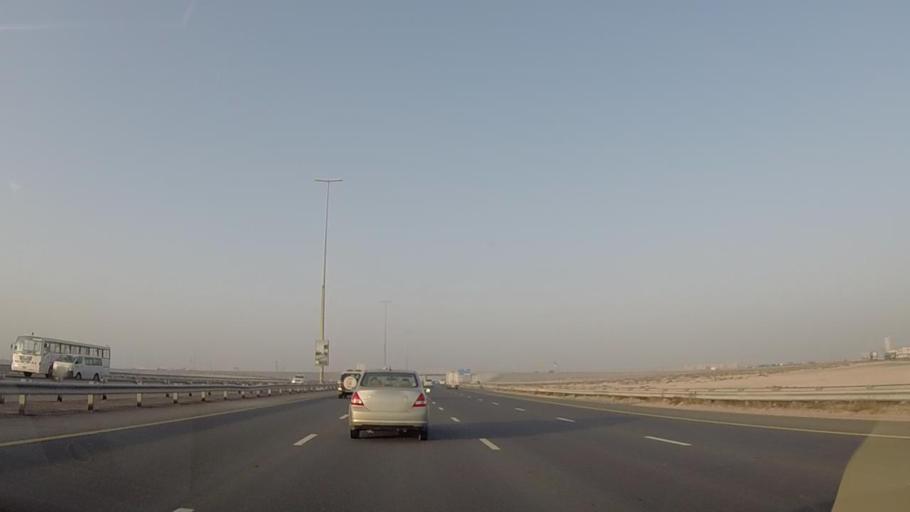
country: AE
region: Dubai
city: Dubai
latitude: 24.9488
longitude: 55.0671
